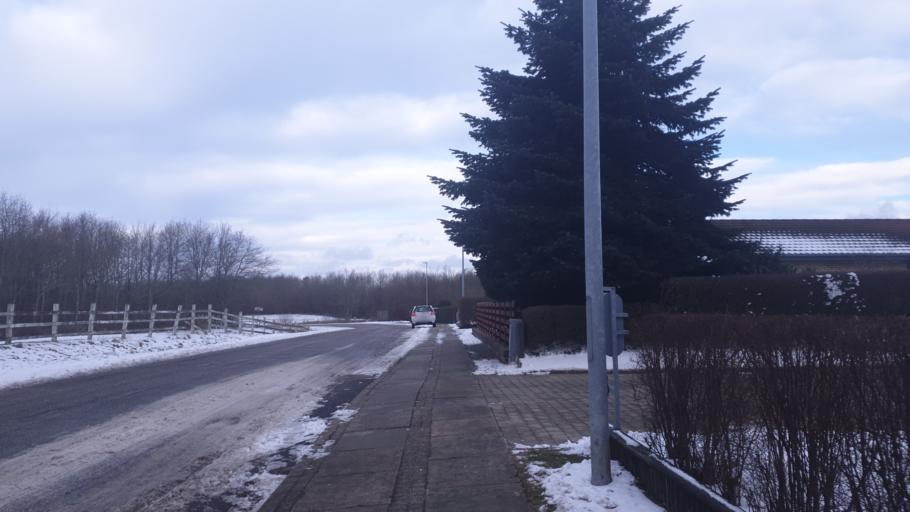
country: DK
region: Central Jutland
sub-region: Hedensted Kommune
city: Hedensted
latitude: 55.7919
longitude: 9.7360
